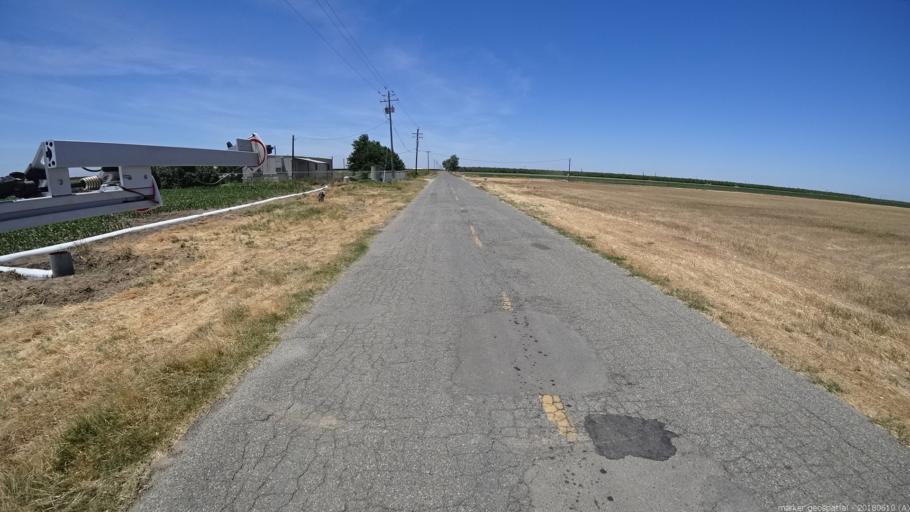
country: US
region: California
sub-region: Madera County
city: Chowchilla
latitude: 37.0544
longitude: -120.3482
